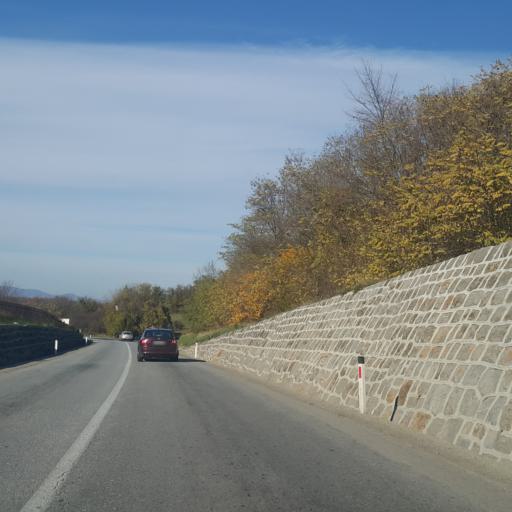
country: RS
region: Central Serbia
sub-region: Sumadijski Okrug
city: Topola
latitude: 44.2655
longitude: 20.6941
